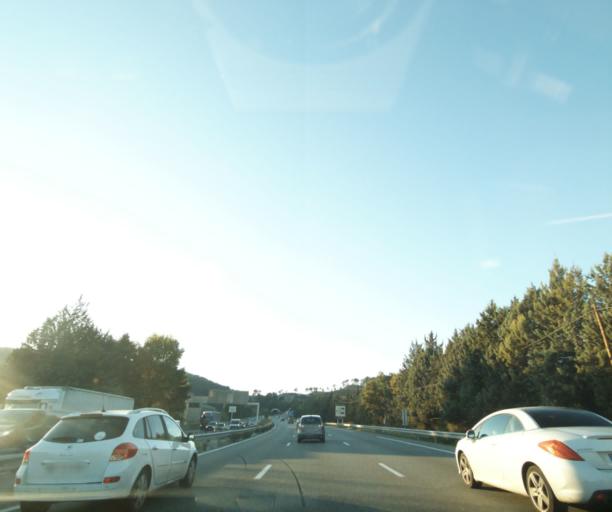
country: FR
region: Provence-Alpes-Cote d'Azur
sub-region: Departement des Bouches-du-Rhone
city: Le Tholonet
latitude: 43.5036
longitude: 5.5164
